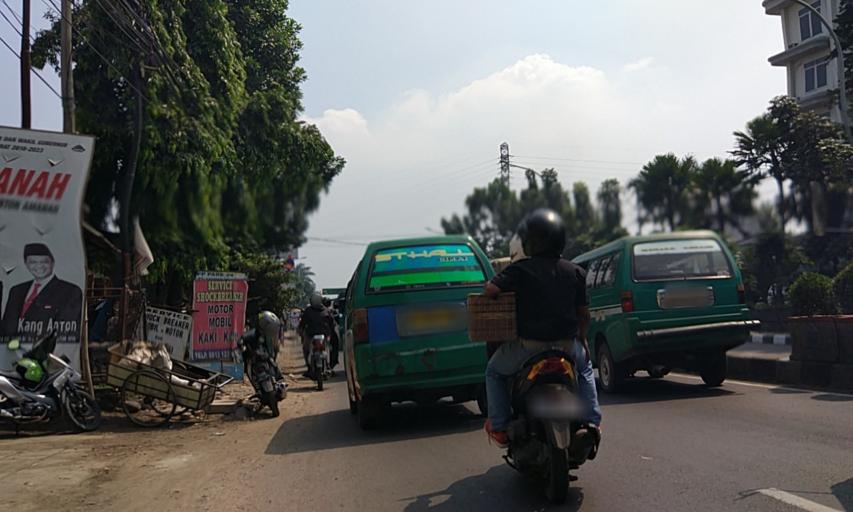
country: ID
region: West Java
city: Cimahi
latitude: -6.9087
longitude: 107.5680
